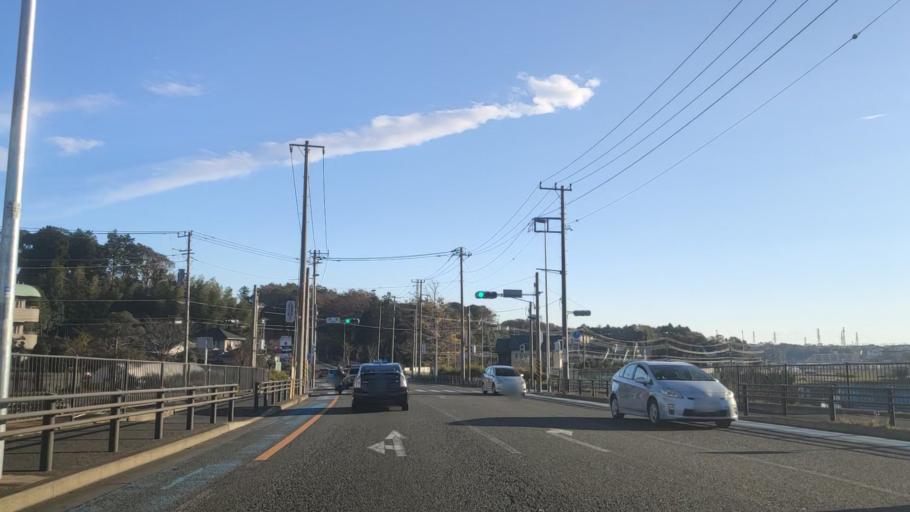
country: JP
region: Kanagawa
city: Fujisawa
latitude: 35.3969
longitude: 139.4861
